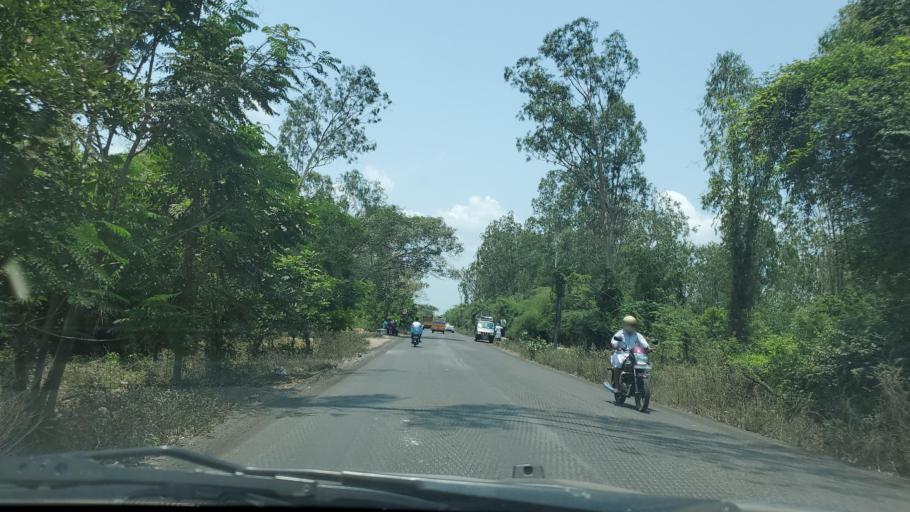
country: IN
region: Tamil Nadu
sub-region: Kancheepuram
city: Vengavasal
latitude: 12.8695
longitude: 80.1750
